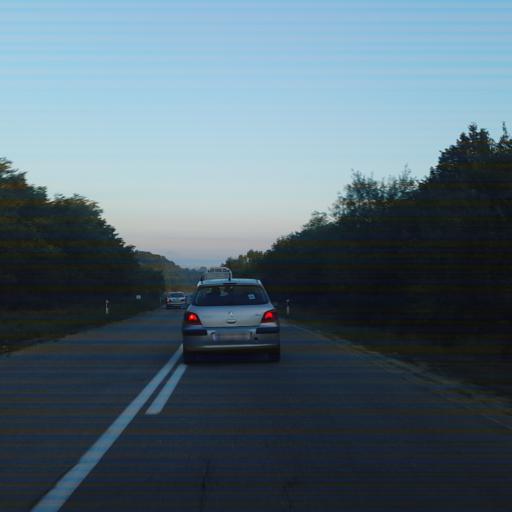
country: RS
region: Central Serbia
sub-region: Zajecarski Okrug
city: Zajecar
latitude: 43.9629
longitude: 22.2984
